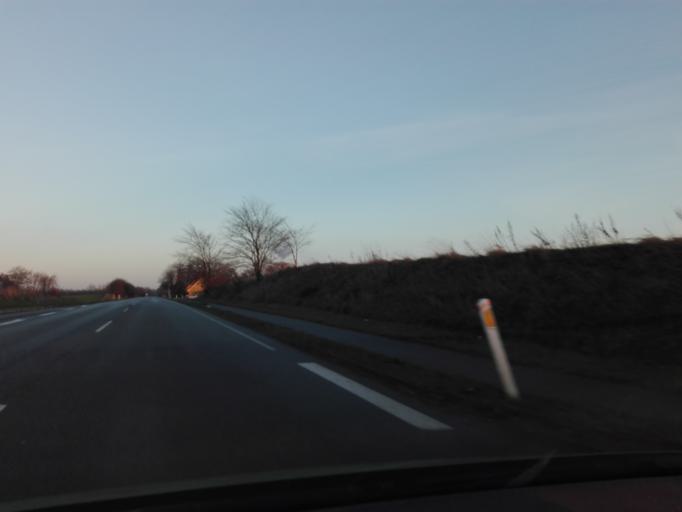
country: DK
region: Central Jutland
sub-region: Skanderborg Kommune
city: Skovby
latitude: 56.1509
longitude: 9.9828
